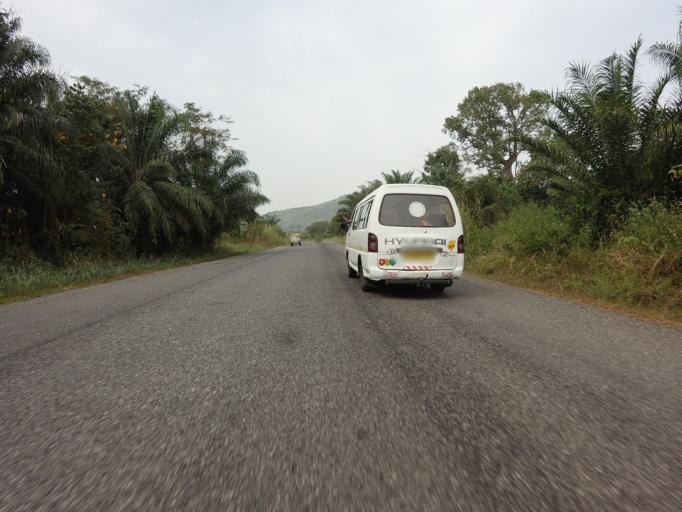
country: GH
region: Volta
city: Ho
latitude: 6.4397
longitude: 0.2000
